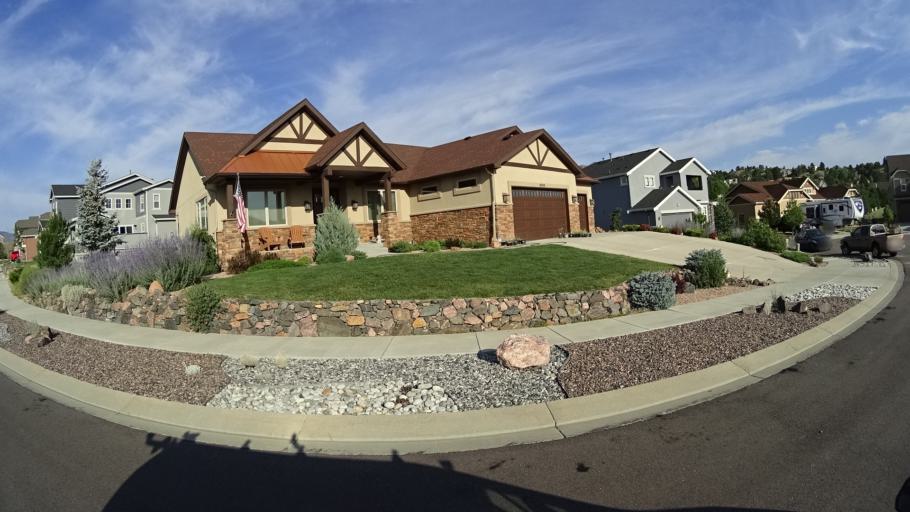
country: US
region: Colorado
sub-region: El Paso County
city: Air Force Academy
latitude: 38.9234
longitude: -104.8459
